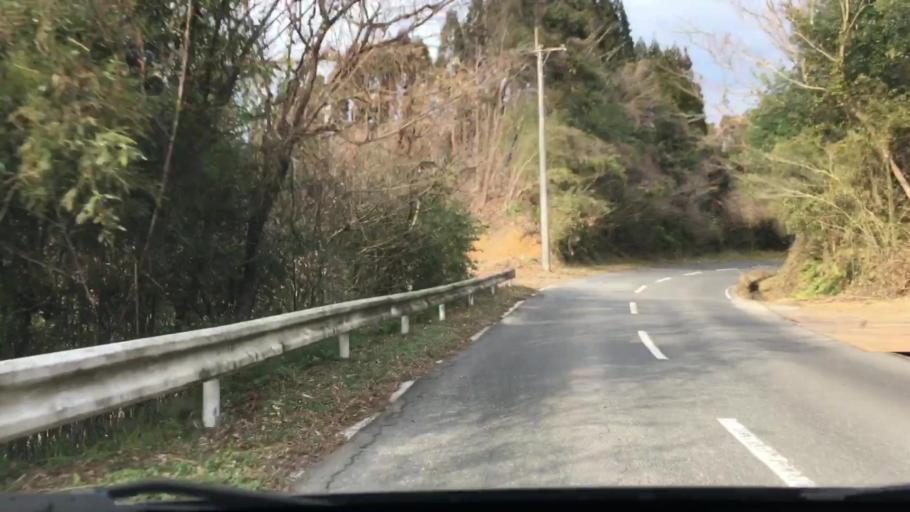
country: JP
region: Miyazaki
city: Nichinan
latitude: 31.6092
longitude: 131.3297
